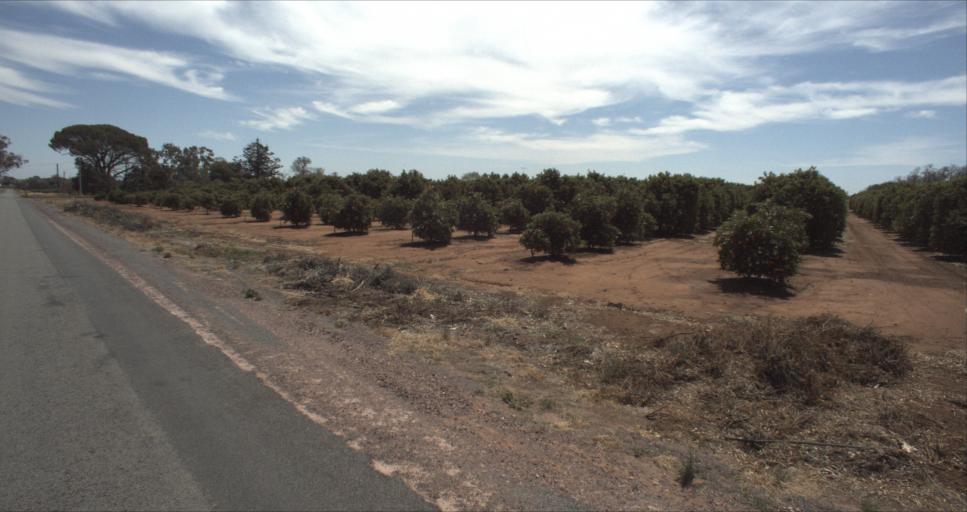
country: AU
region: New South Wales
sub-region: Leeton
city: Leeton
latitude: -34.6149
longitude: 146.4333
